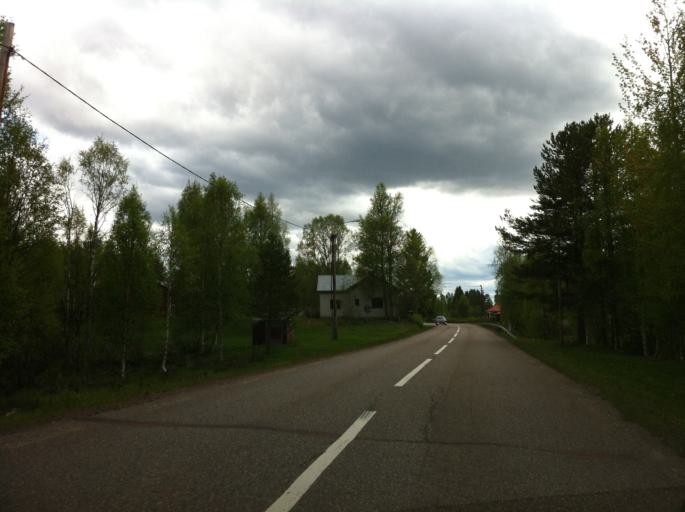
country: NO
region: Hedmark
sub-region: Trysil
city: Innbygda
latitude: 61.4210
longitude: 13.0861
